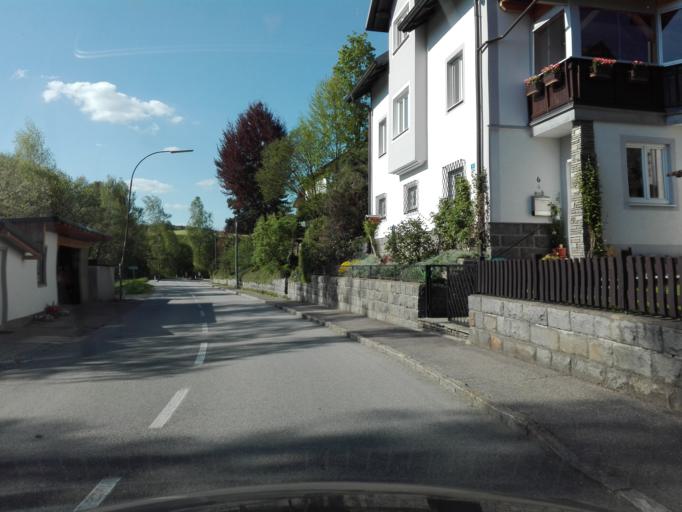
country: DE
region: Bavaria
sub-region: Lower Bavaria
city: Obernzell
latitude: 48.4851
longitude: 13.5738
